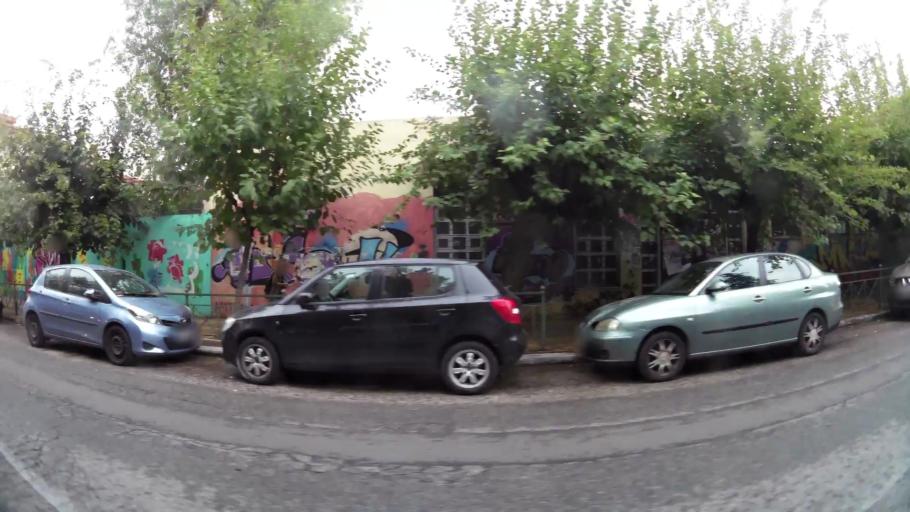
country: GR
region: Attica
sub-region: Nomarchia Athinas
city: Vyronas
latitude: 37.9693
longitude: 23.7473
